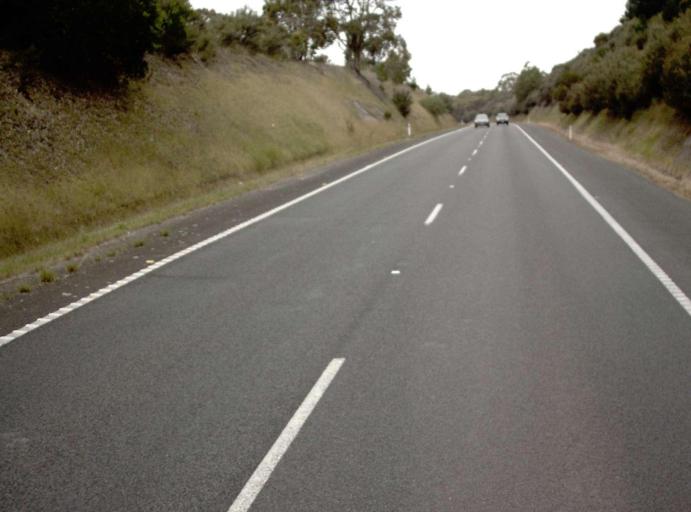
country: AU
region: Victoria
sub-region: Latrobe
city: Moe
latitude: -38.2050
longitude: 146.3000
